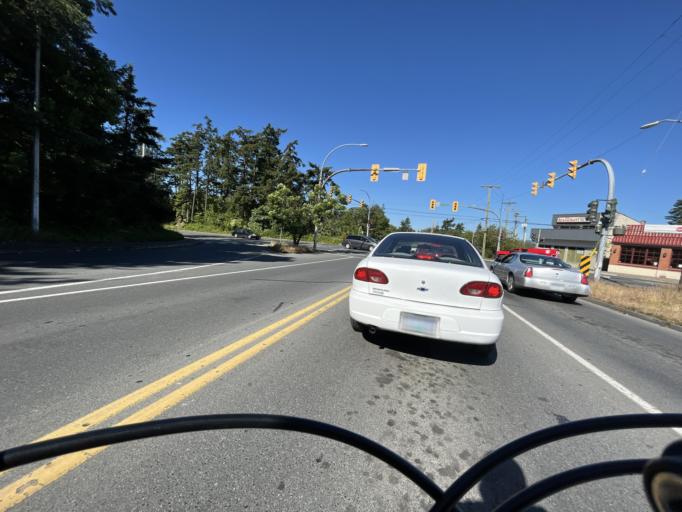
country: CA
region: British Columbia
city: Victoria
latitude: 48.4477
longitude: -123.4000
